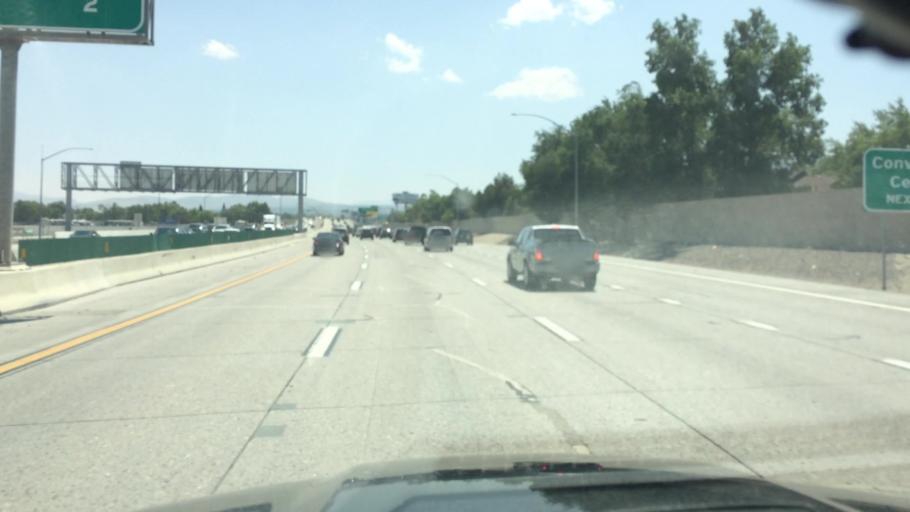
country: US
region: Nevada
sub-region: Washoe County
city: Reno
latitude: 39.4993
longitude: -119.7837
